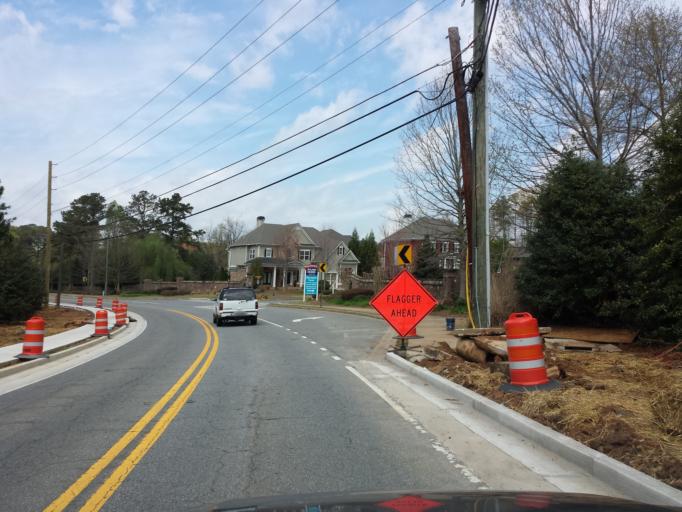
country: US
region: Georgia
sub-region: Cherokee County
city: Woodstock
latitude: 34.0310
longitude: -84.4956
